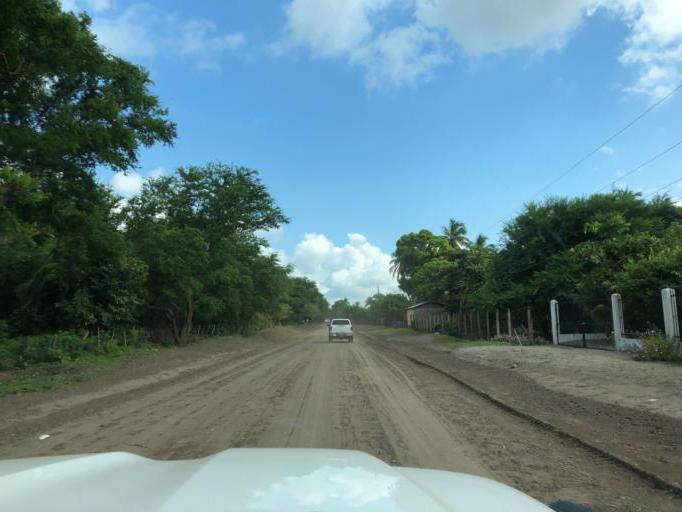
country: NI
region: Granada
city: Granada
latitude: 11.9986
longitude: -85.9359
